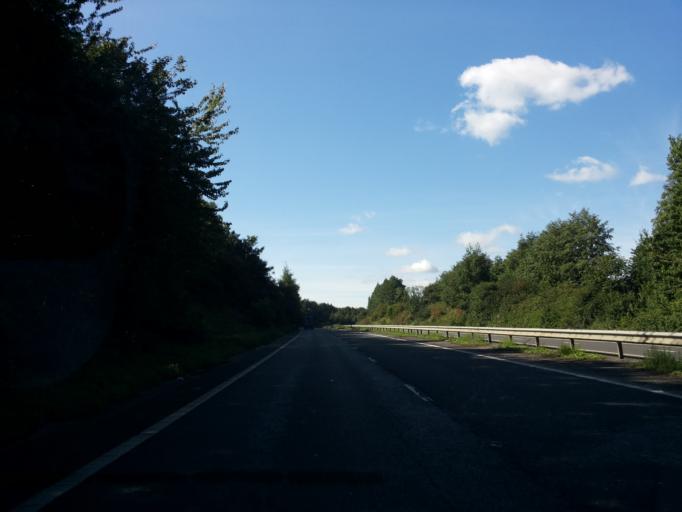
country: GB
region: England
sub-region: Kent
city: Canterbury
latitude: 51.2549
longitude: 1.0979
